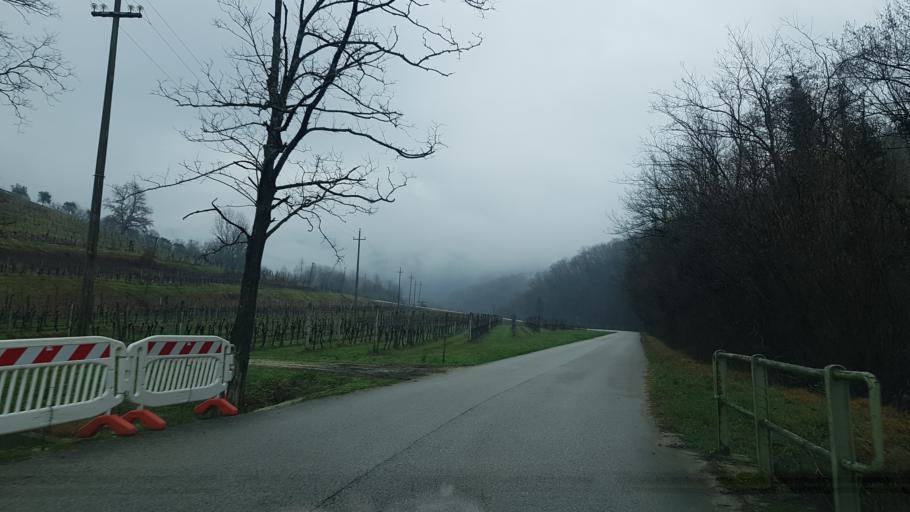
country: IT
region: Friuli Venezia Giulia
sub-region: Provincia di Udine
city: Prepotto
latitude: 46.0750
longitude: 13.4744
